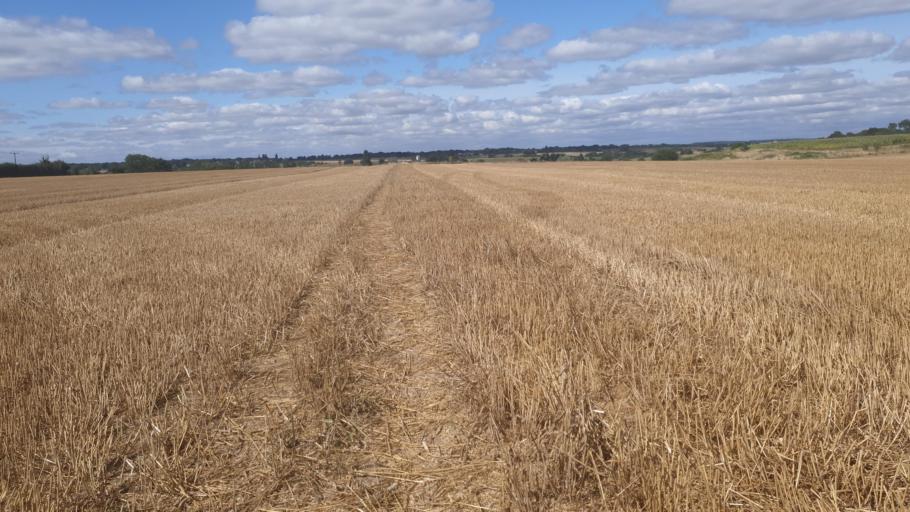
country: GB
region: England
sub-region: Essex
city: Dovercourt
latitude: 51.9191
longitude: 1.2207
